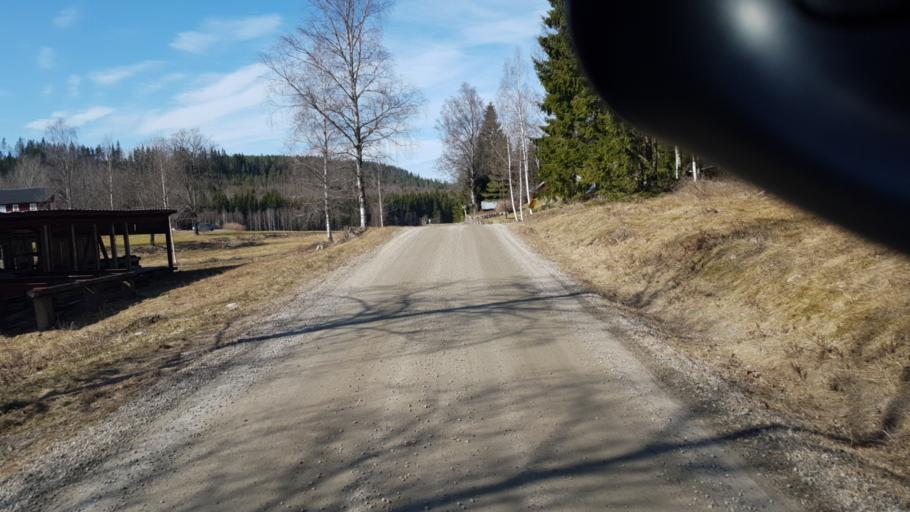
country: SE
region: Vaermland
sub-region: Sunne Kommun
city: Sunne
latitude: 59.7078
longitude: 12.8783
